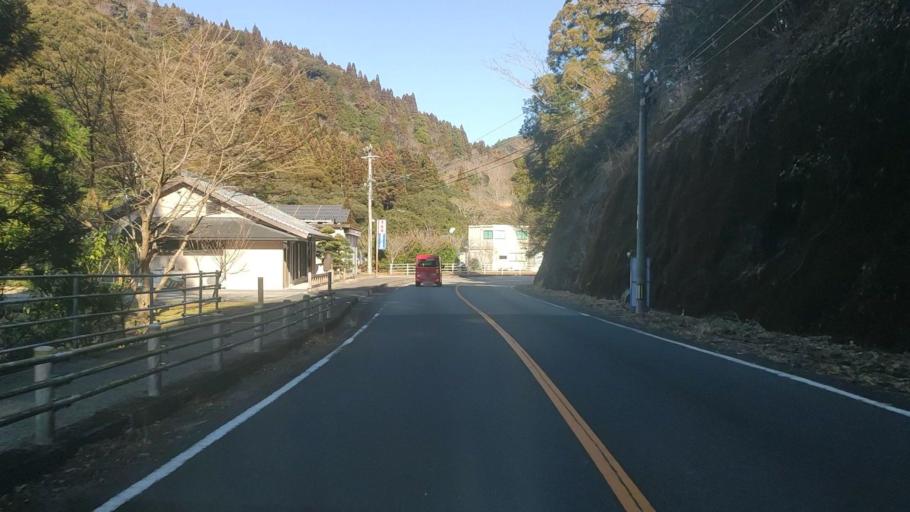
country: JP
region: Oita
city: Saiki
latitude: 32.7683
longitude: 131.8037
